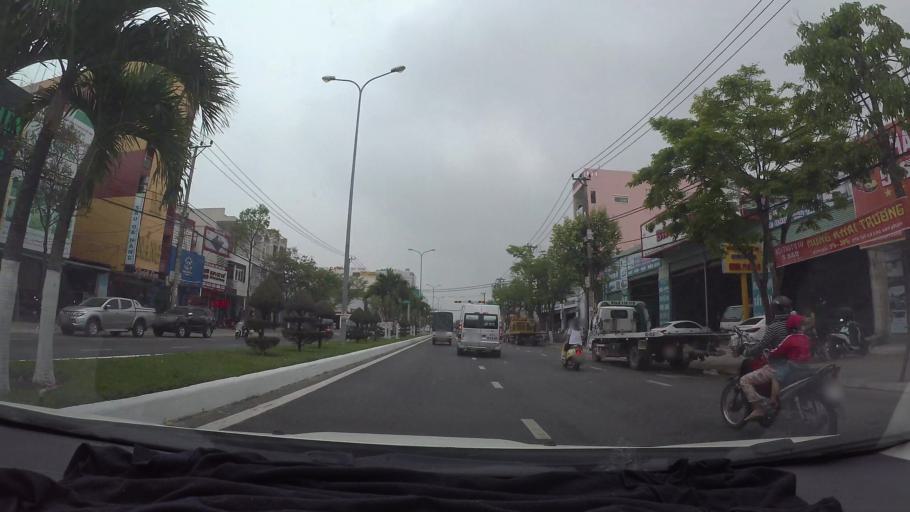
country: VN
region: Da Nang
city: Cam Le
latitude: 16.0333
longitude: 108.2091
